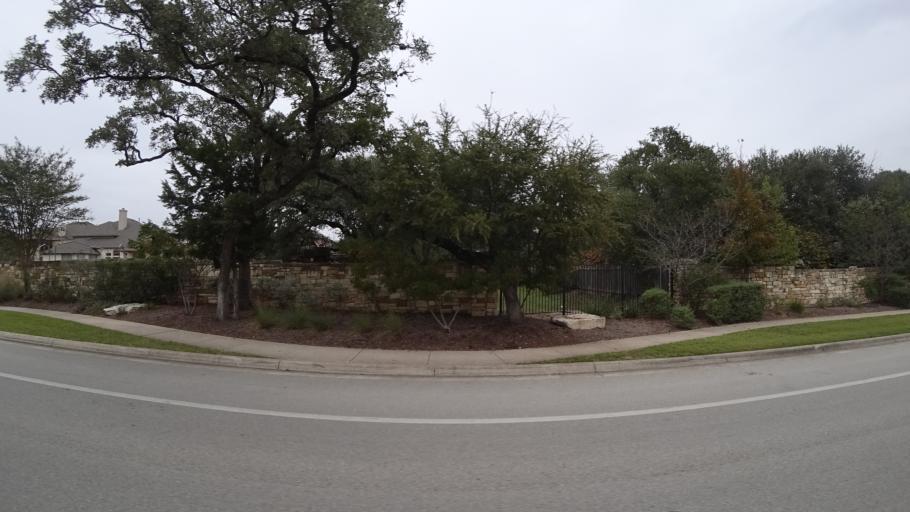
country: US
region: Texas
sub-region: Travis County
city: Shady Hollow
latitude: 30.1967
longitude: -97.9153
